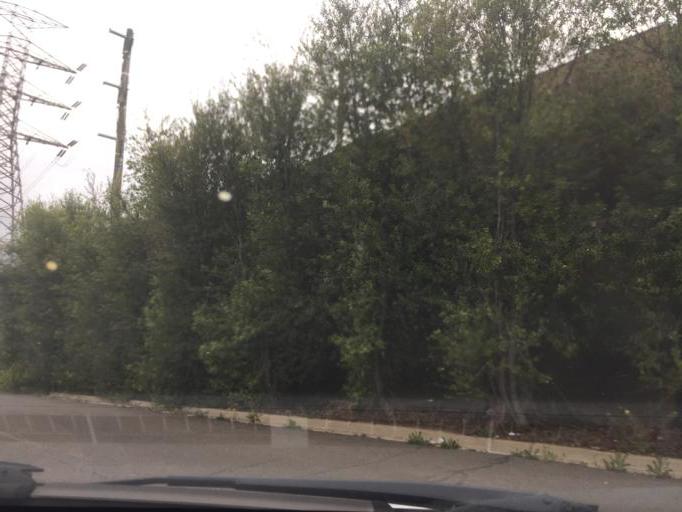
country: AU
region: Victoria
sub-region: Hobsons Bay
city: South Kingsville
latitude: -37.8244
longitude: 144.8774
